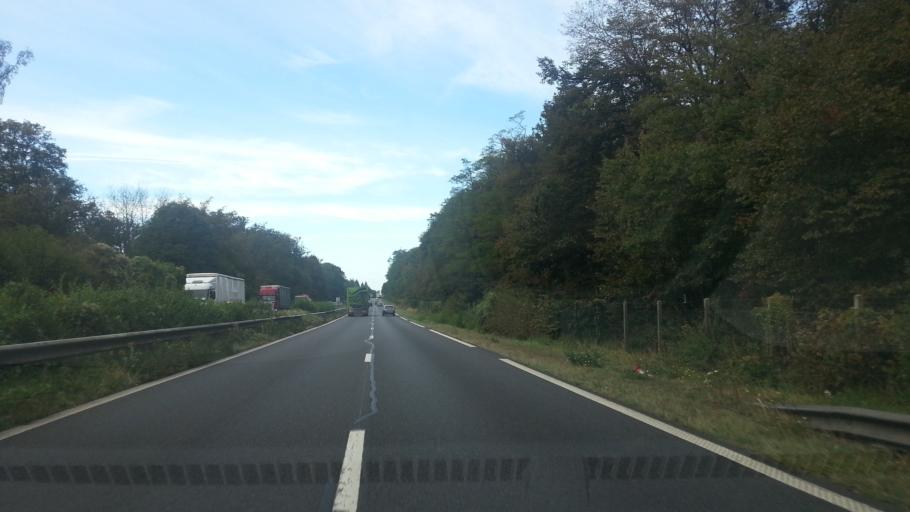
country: FR
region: Picardie
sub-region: Departement de l'Oise
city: Avilly-Saint-Leonard
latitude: 49.2230
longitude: 2.5476
